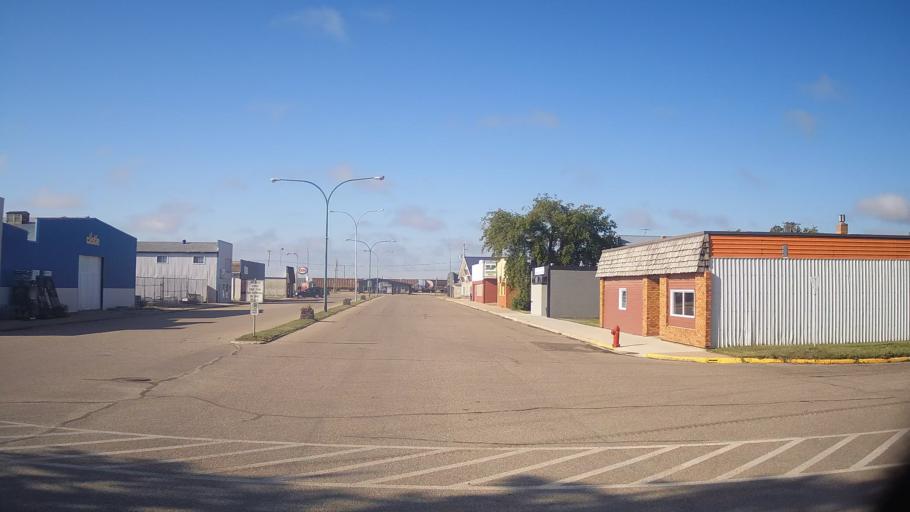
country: CA
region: Saskatchewan
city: Lanigan
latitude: 51.8471
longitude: -105.0331
